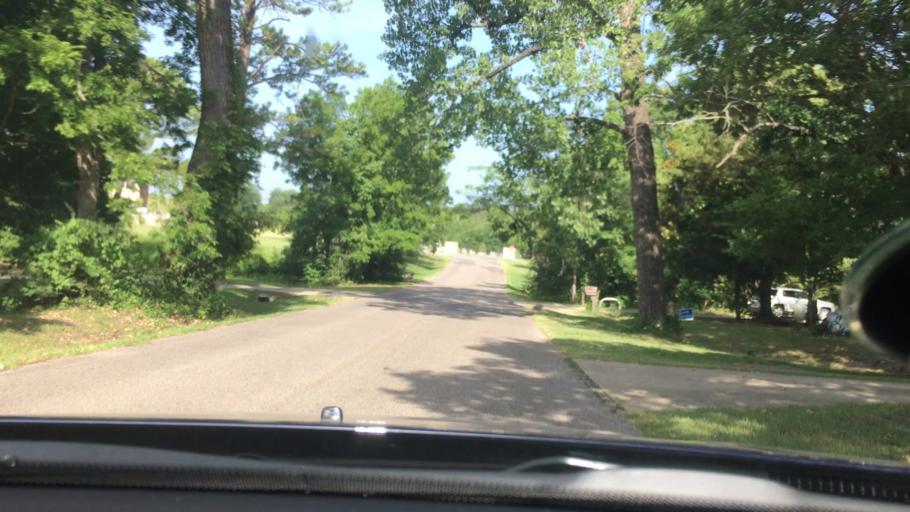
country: US
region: Oklahoma
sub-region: Pontotoc County
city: Ada
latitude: 34.7569
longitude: -96.6581
